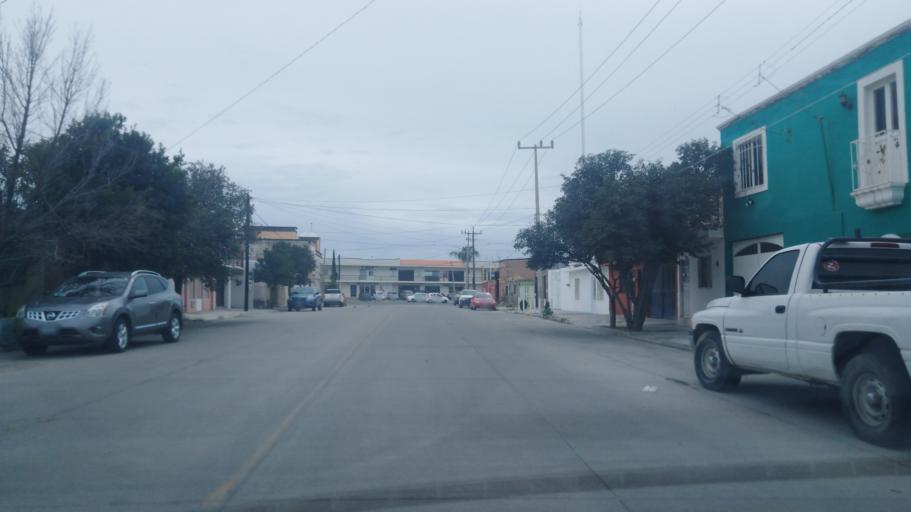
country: MX
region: Durango
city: Victoria de Durango
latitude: 24.0280
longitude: -104.6265
